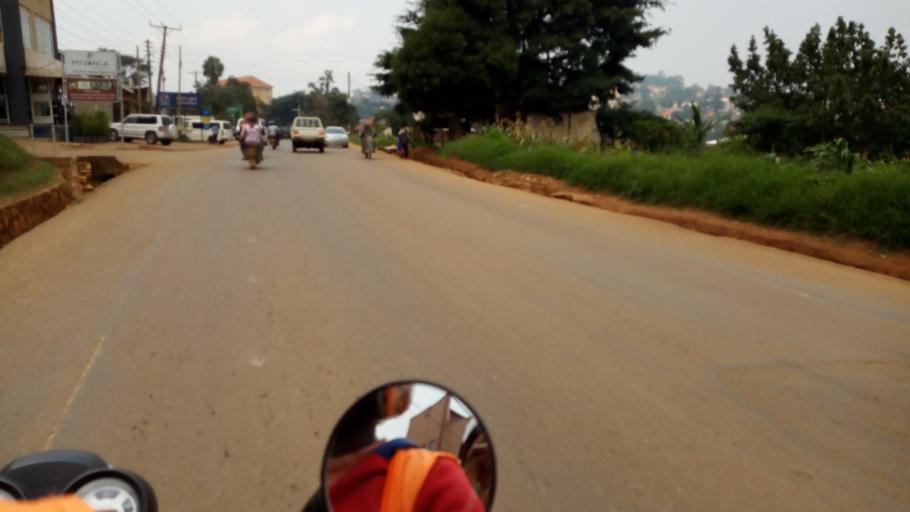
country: UG
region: Central Region
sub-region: Wakiso District
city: Kireka
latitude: 0.3190
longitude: 32.6313
